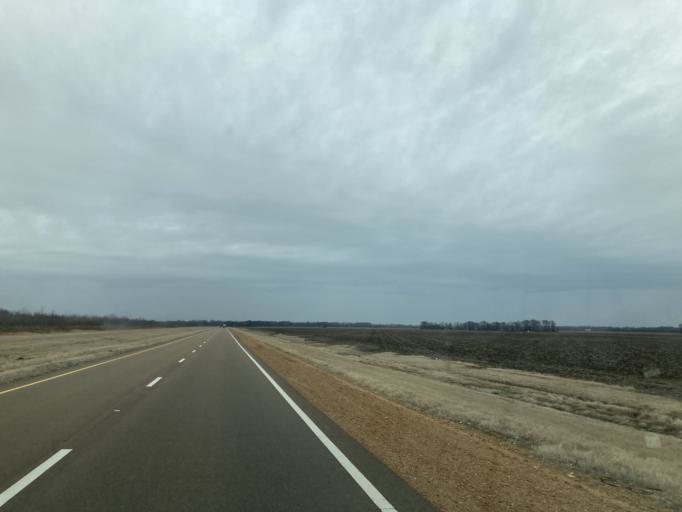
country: US
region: Mississippi
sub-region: Humphreys County
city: Belzoni
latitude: 33.0578
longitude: -90.4698
